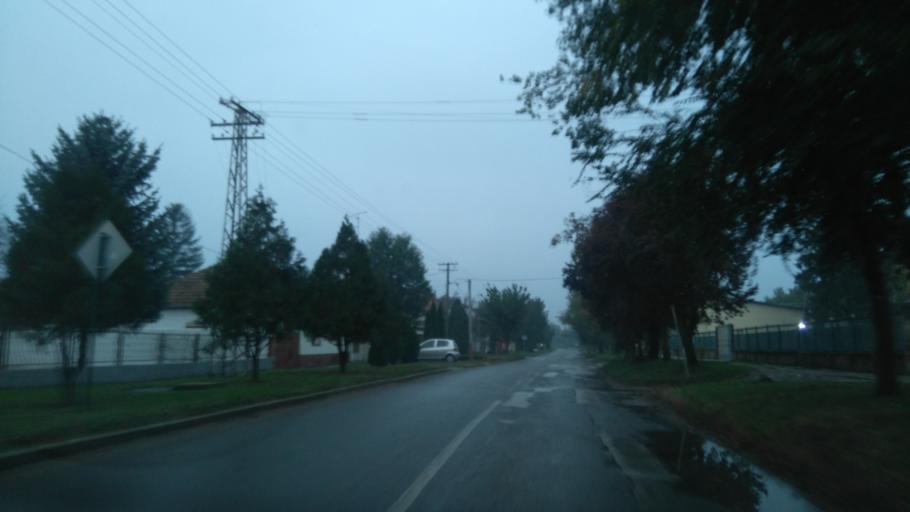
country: RS
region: Autonomna Pokrajina Vojvodina
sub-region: Juznobacki Okrug
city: Becej
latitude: 45.6265
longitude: 20.0383
